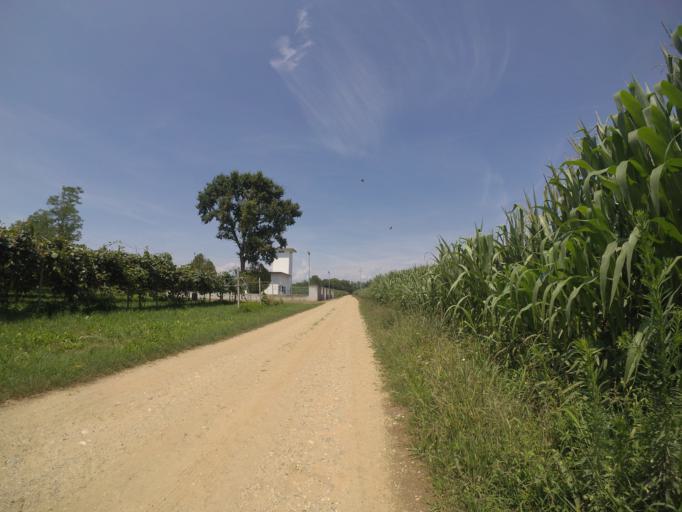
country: IT
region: Friuli Venezia Giulia
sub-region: Provincia di Udine
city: Bertiolo
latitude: 45.9723
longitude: 13.0957
